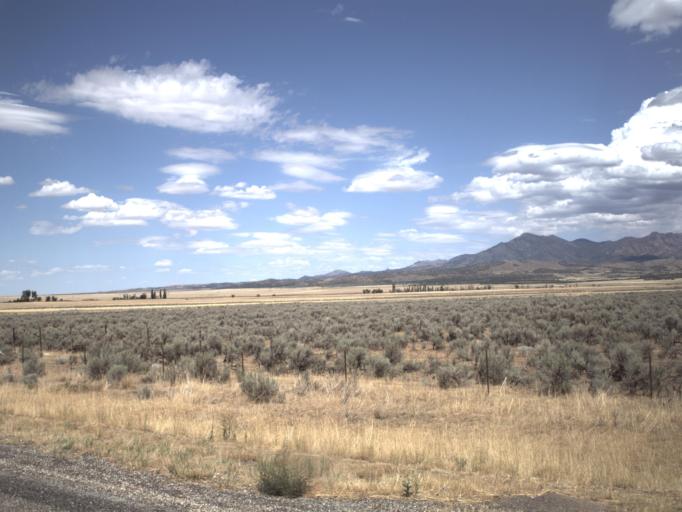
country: US
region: Utah
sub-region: Millard County
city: Fillmore
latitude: 39.1123
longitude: -112.2752
